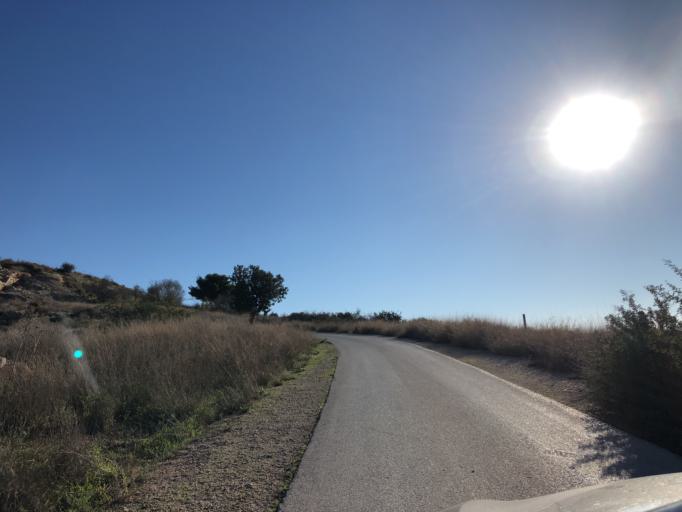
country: PS
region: West Bank
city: Idhna
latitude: 31.5948
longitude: 34.8977
